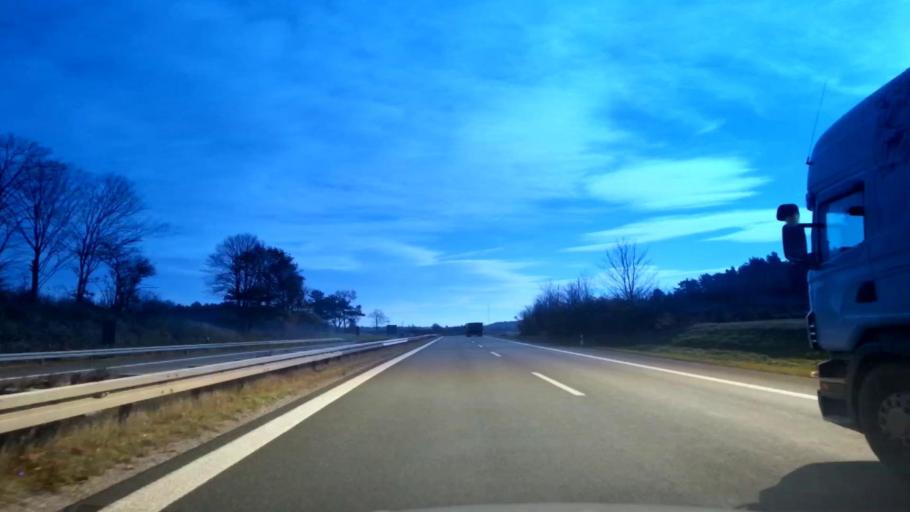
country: DE
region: Bavaria
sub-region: Upper Franconia
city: Kasendorf
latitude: 50.0107
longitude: 11.3271
